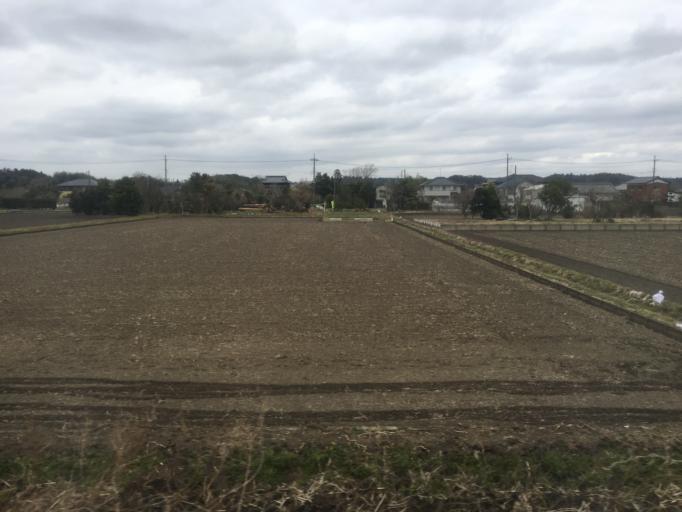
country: JP
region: Chiba
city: Oami
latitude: 35.5395
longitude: 140.3339
